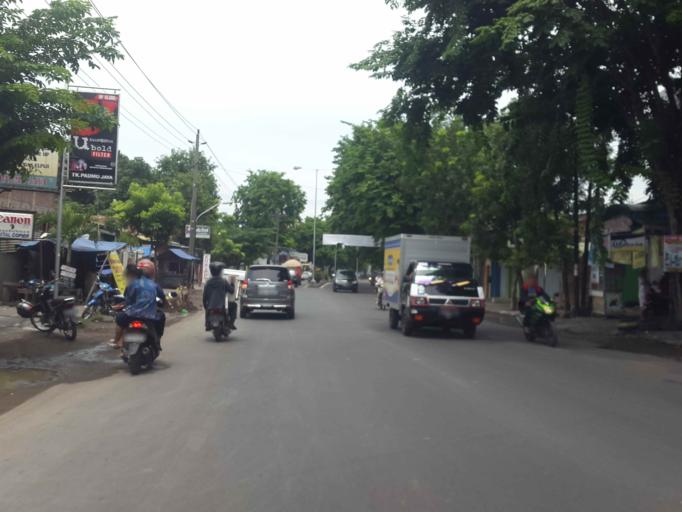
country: ID
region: Central Java
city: Mranggen
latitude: -7.0145
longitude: 110.4720
